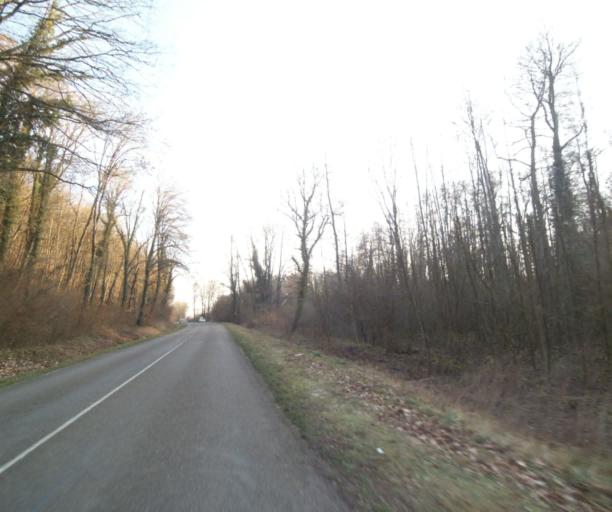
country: FR
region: Champagne-Ardenne
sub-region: Departement de la Haute-Marne
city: Chevillon
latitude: 48.5307
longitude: 5.1073
